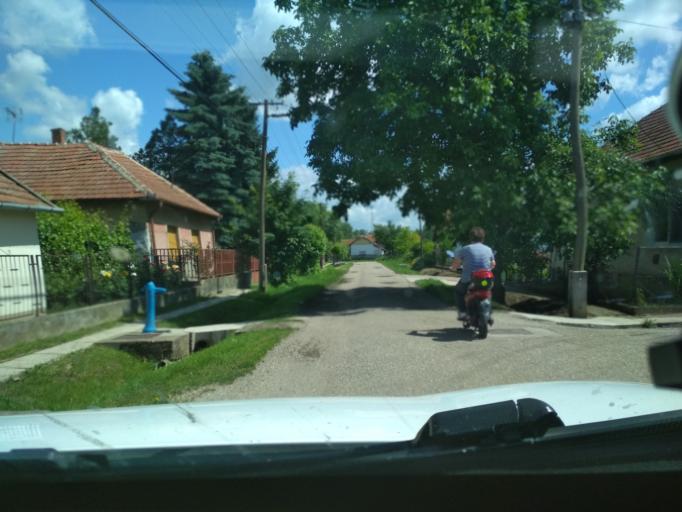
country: HU
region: Jasz-Nagykun-Szolnok
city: Abadszalok
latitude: 47.4812
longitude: 20.5999
